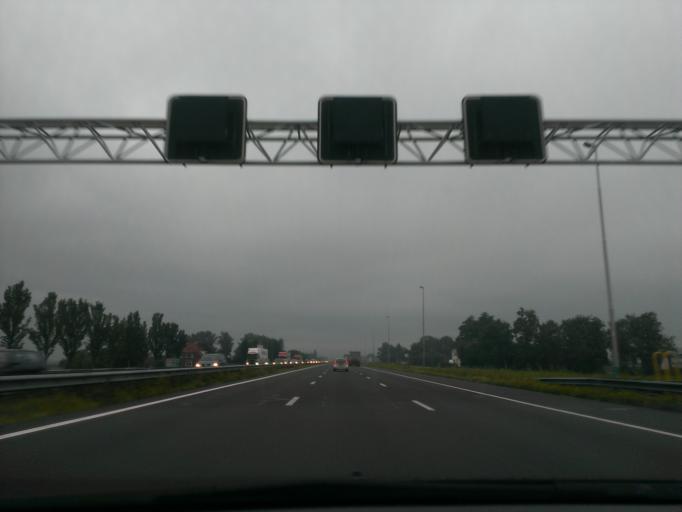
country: NL
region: Overijssel
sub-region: Gemeente Zwartewaterland
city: Hasselt
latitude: 52.5584
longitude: 6.1771
